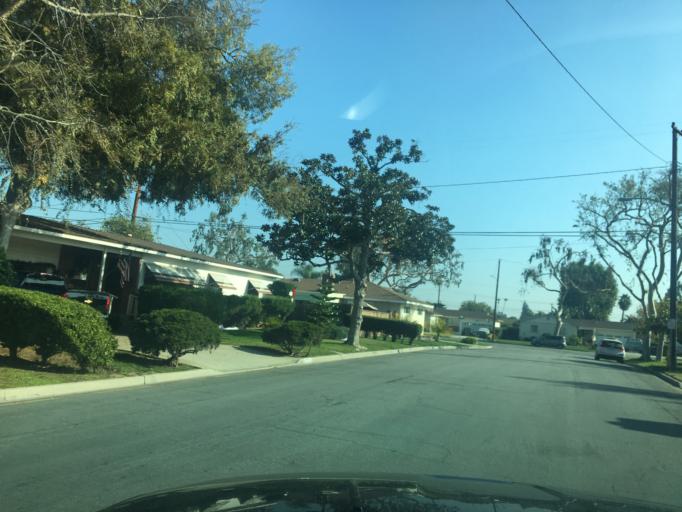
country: US
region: California
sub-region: Orange County
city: Tustin
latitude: 33.7355
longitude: -117.8224
